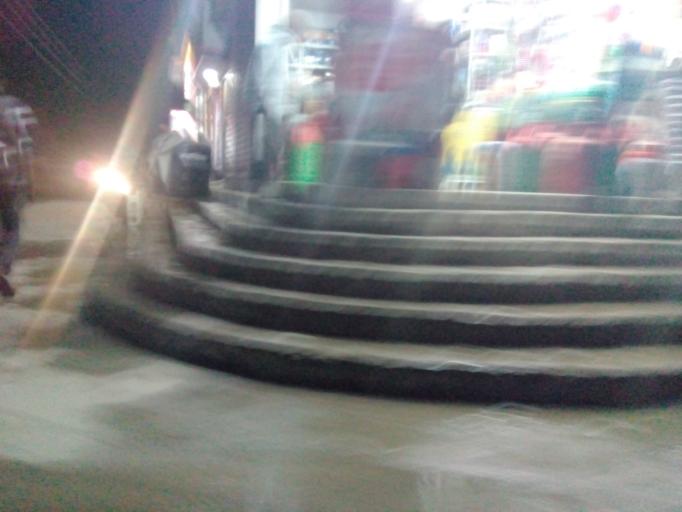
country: BD
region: Dhaka
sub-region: Dhaka
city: Dhaka
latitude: 23.6967
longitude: 90.4752
